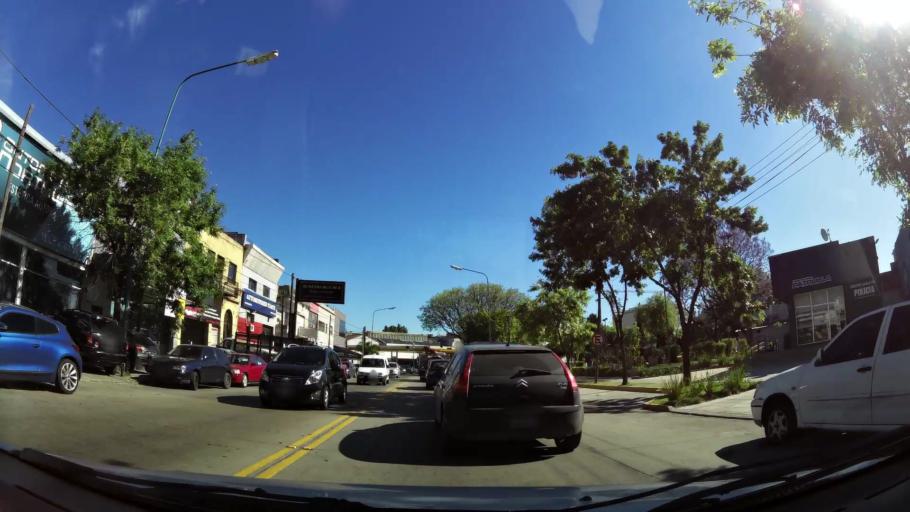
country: AR
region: Buenos Aires
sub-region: Partido de General San Martin
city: General San Martin
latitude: -34.5468
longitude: -58.5000
